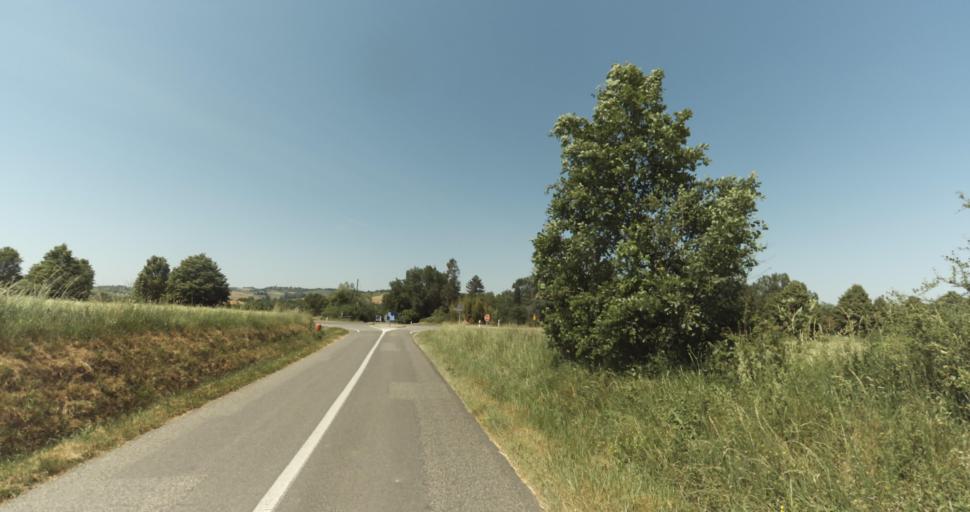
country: FR
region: Midi-Pyrenees
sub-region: Departement de la Haute-Garonne
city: Levignac
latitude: 43.6524
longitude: 1.1752
